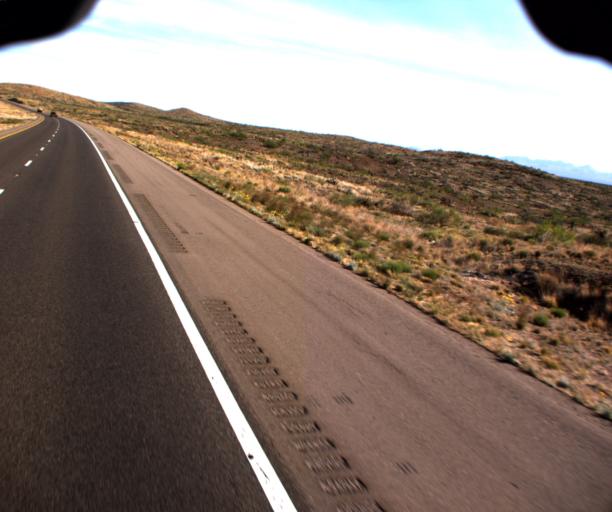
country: US
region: Arizona
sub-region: Cochise County
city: Willcox
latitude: 32.4445
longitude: -109.6634
